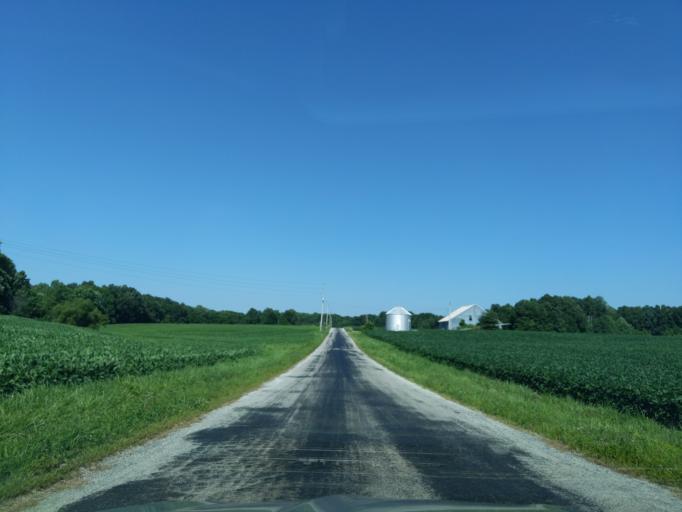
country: US
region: Indiana
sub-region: Ripley County
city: Osgood
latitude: 39.1114
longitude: -85.4323
